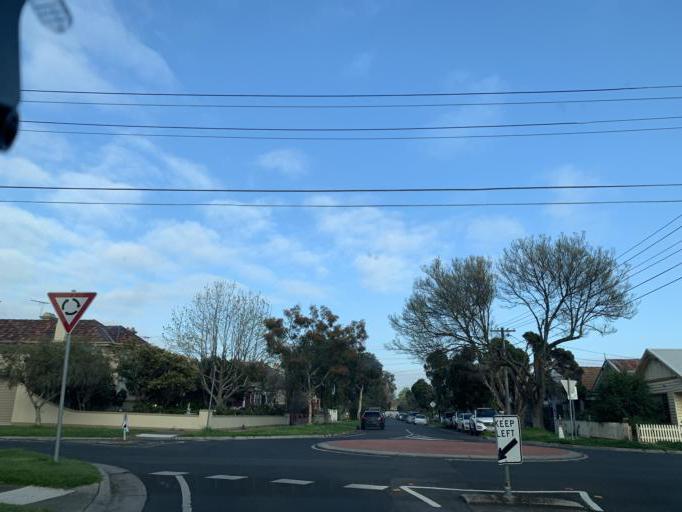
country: AU
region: Victoria
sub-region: Moreland
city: Coburg
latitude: -37.7482
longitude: 144.9687
